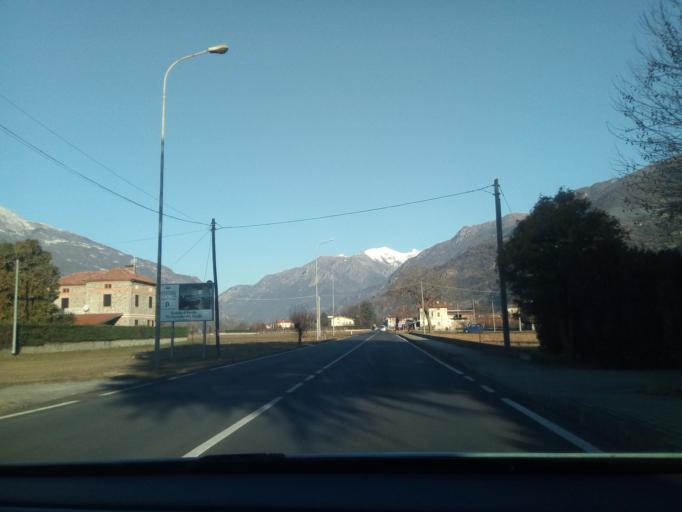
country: IT
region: Piedmont
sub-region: Provincia di Torino
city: Borgofranco d'Ivrea
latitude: 45.5203
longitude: 7.8531
